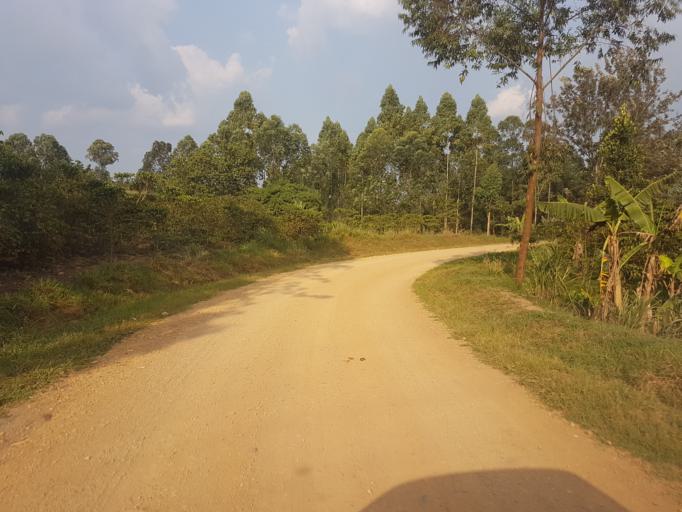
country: UG
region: Western Region
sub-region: Rukungiri District
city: Rukungiri
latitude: -0.6504
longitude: 29.8515
